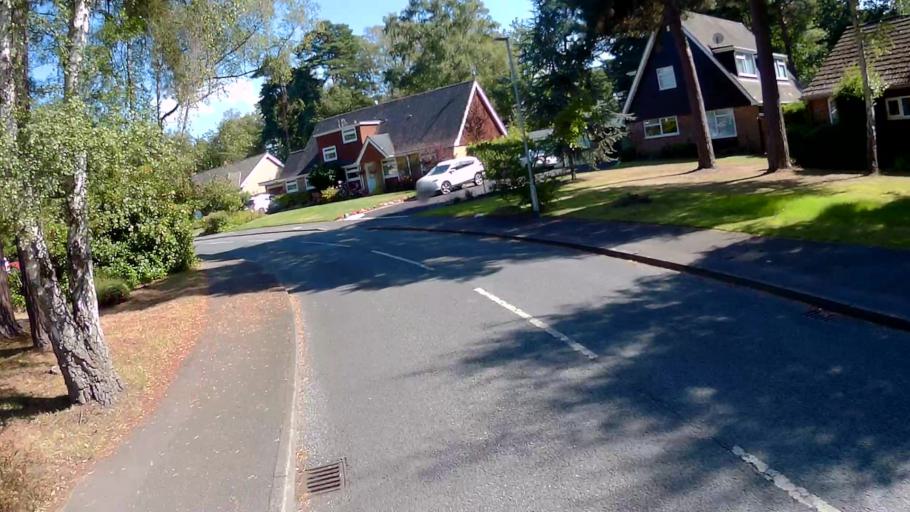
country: GB
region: England
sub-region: Bracknell Forest
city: Crowthorne
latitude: 51.3731
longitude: -0.8070
